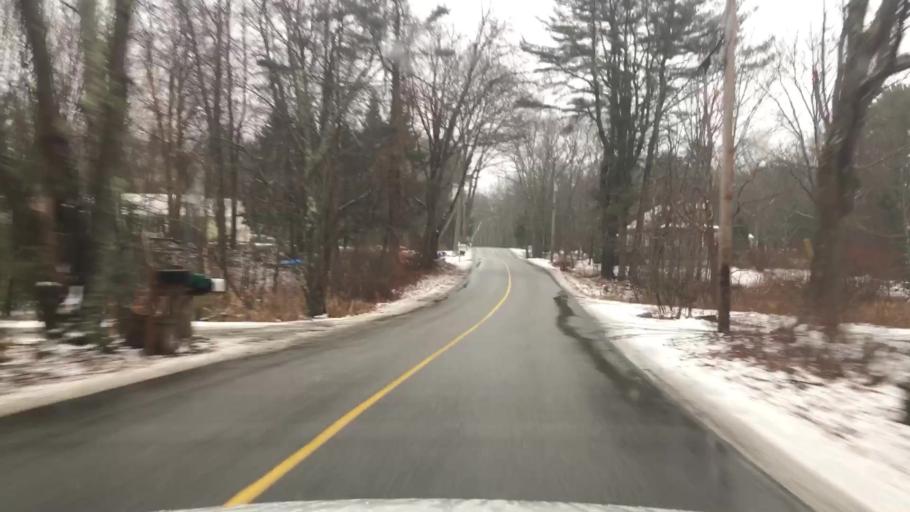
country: US
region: Maine
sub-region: York County
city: Arundel
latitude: 43.3741
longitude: -70.4560
